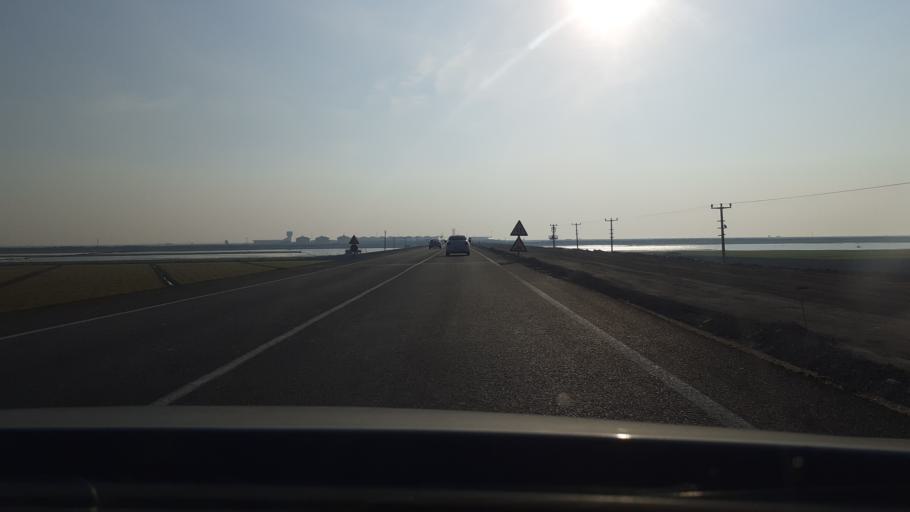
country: TR
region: Hatay
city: Serinyol
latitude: 36.3676
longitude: 36.2628
